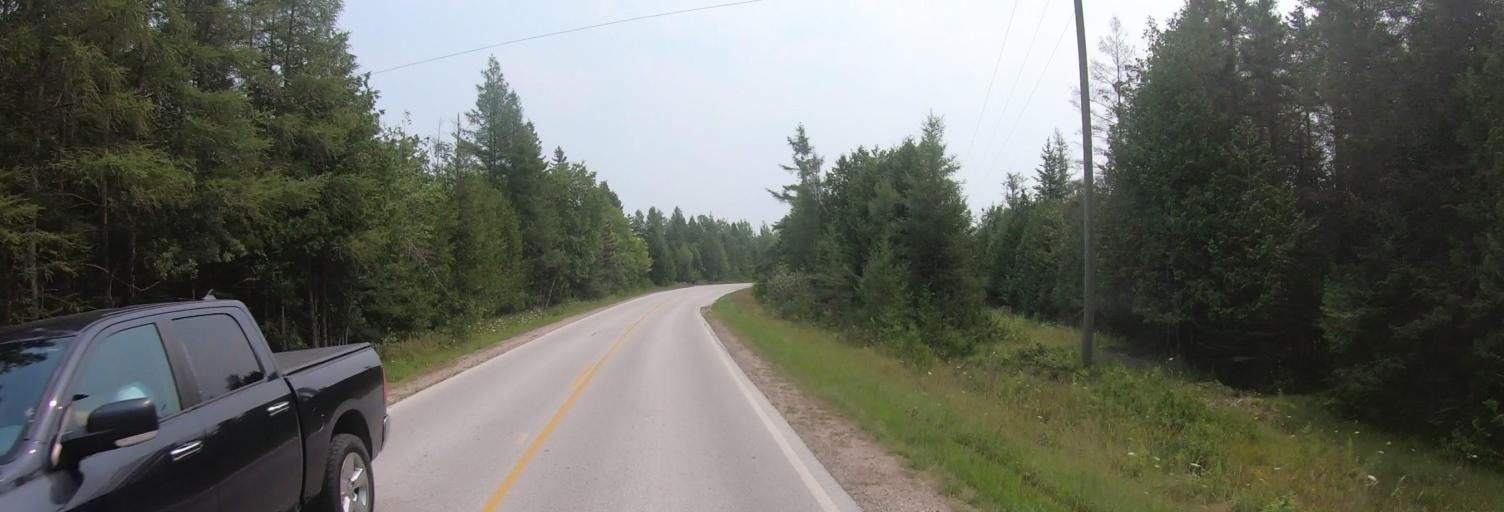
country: CA
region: Ontario
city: Thessalon
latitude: 45.9837
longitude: -83.6793
